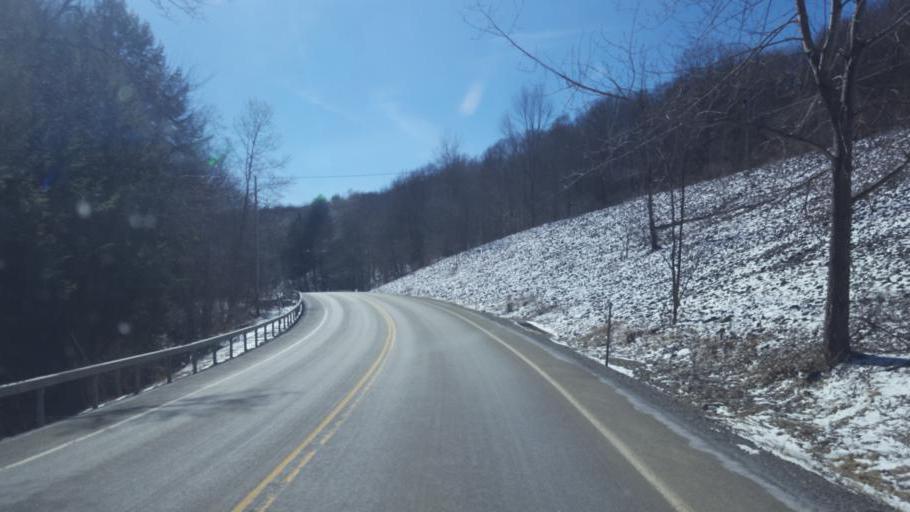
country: US
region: New York
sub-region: Allegany County
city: Andover
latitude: 42.0531
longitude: -77.7936
